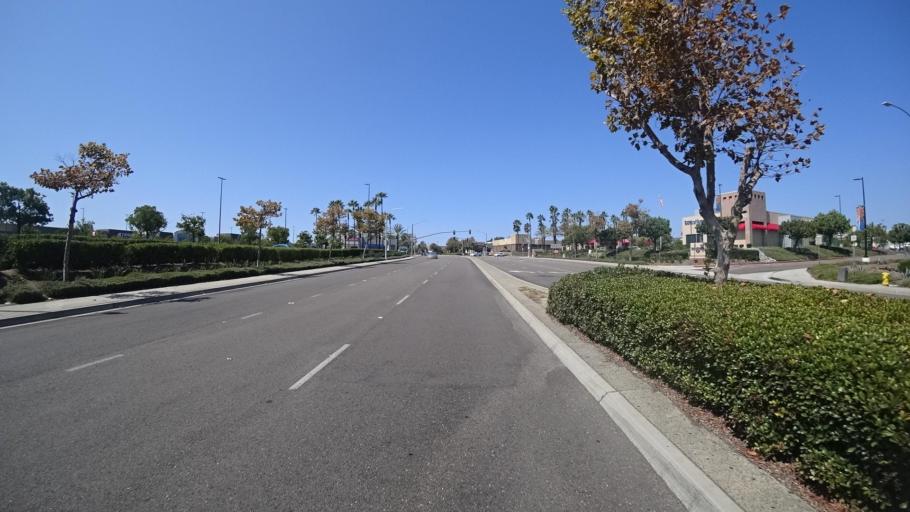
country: US
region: California
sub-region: San Diego County
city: Vista
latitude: 33.1702
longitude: -117.2143
